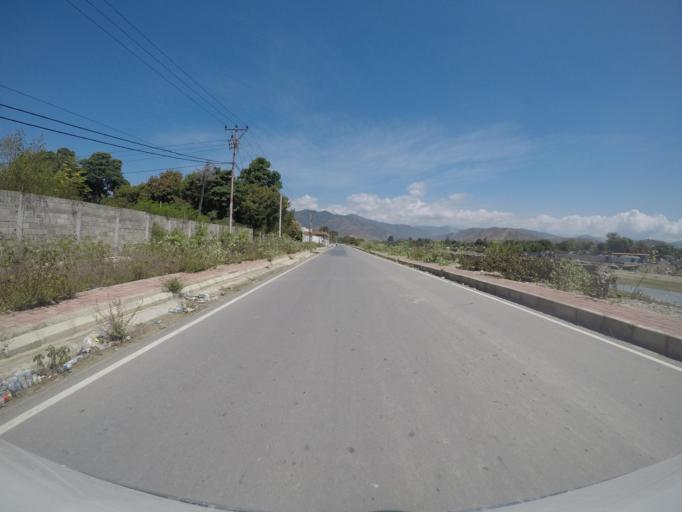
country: TL
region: Dili
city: Dili
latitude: -8.5418
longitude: 125.5356
